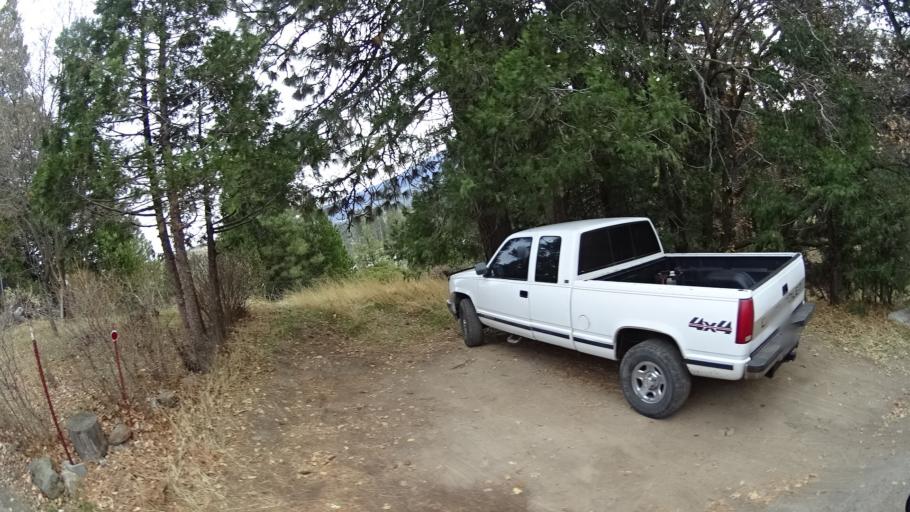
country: US
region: California
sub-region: Siskiyou County
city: Weed
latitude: 41.4183
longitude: -122.3851
